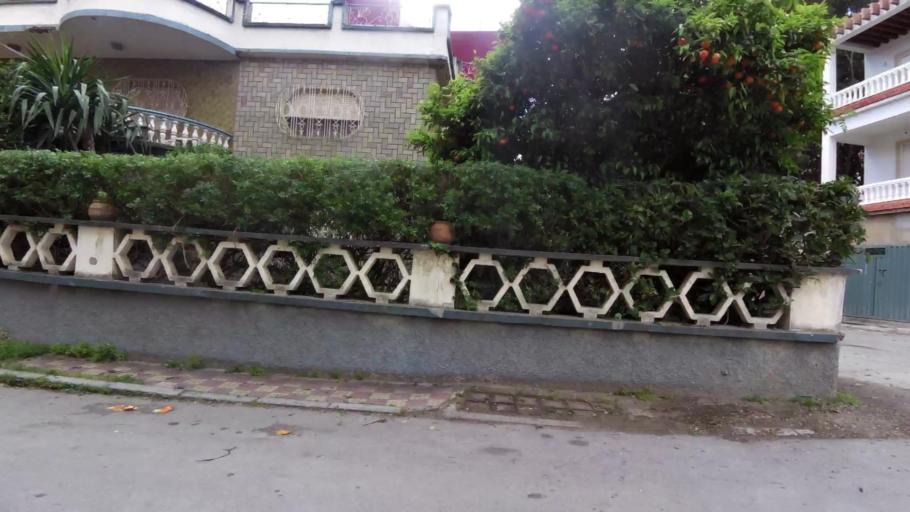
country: MA
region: Tanger-Tetouan
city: Tetouan
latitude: 35.5815
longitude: -5.3505
